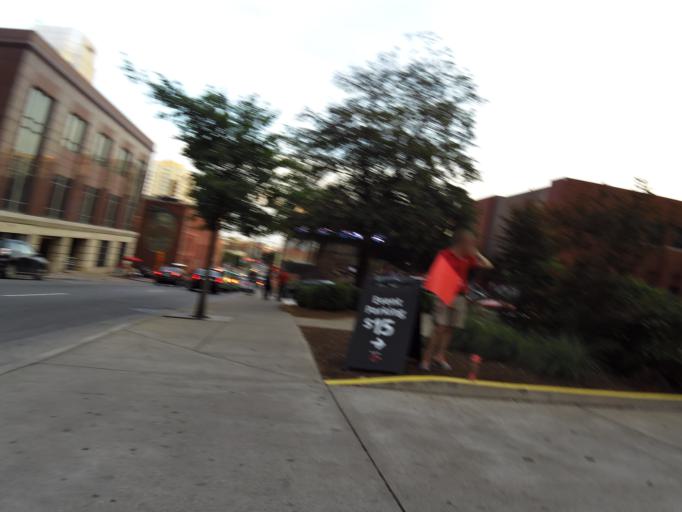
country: US
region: Tennessee
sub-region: Davidson County
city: Nashville
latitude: 36.1620
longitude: -86.7780
